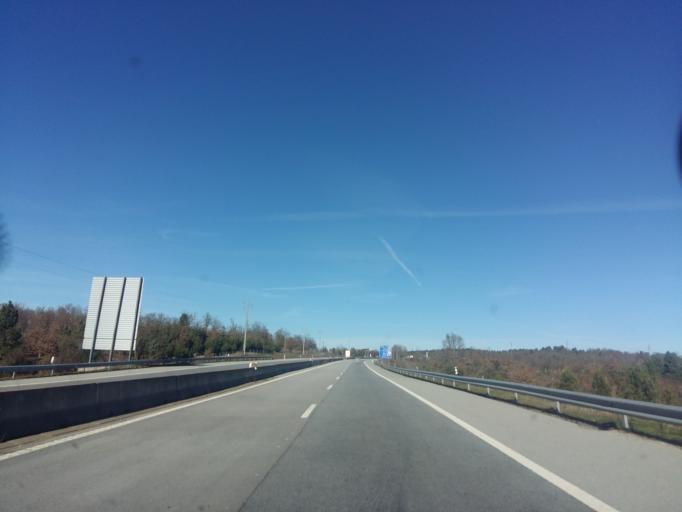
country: PT
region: Guarda
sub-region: Guarda
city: Sequeira
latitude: 40.5349
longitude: -7.2175
